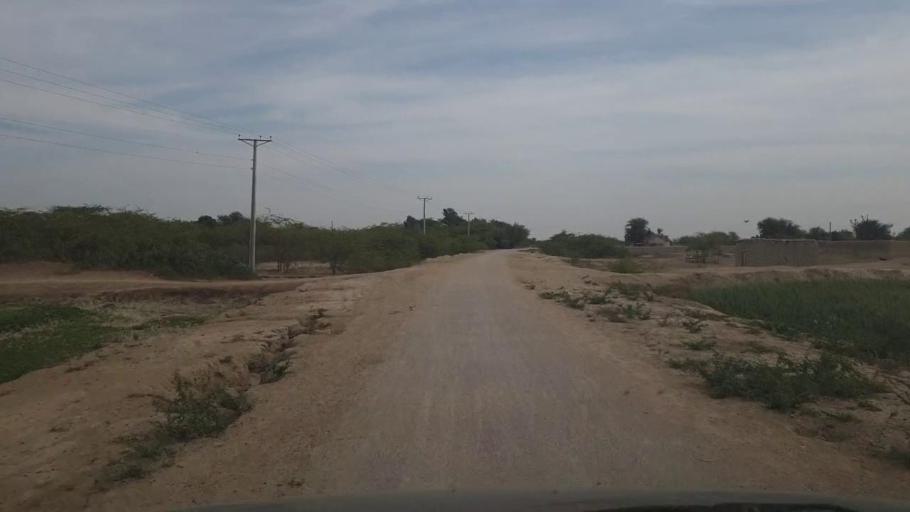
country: PK
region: Sindh
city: Kunri
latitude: 25.2536
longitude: 69.6281
